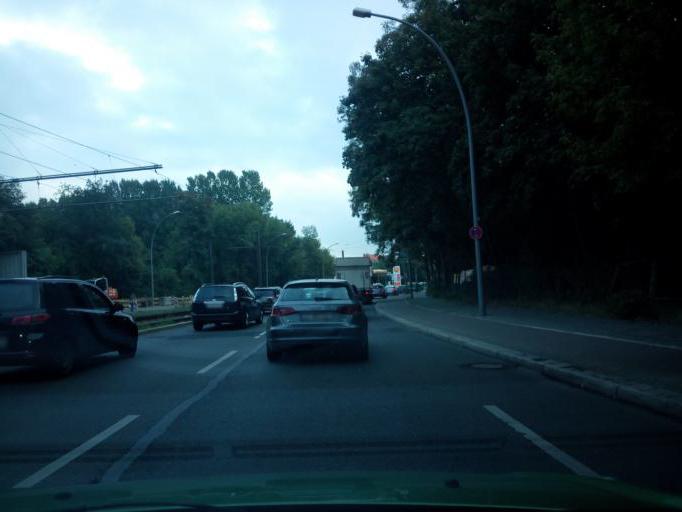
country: DE
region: Berlin
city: Kopenick Bezirk
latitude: 52.4561
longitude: 13.5654
